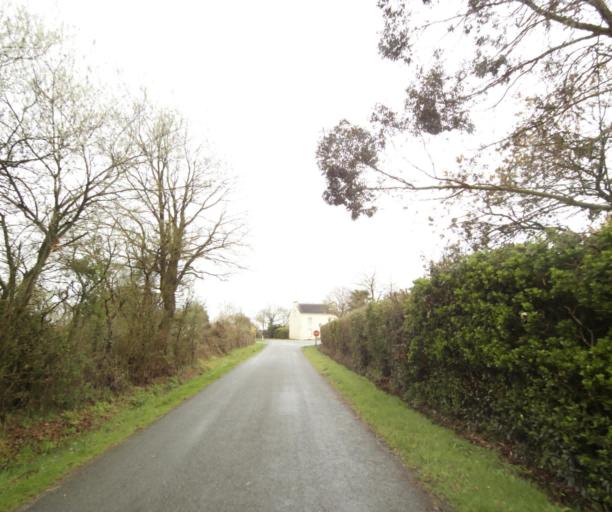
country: FR
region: Pays de la Loire
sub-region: Departement de la Loire-Atlantique
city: Bouvron
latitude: 47.4391
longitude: -1.8517
